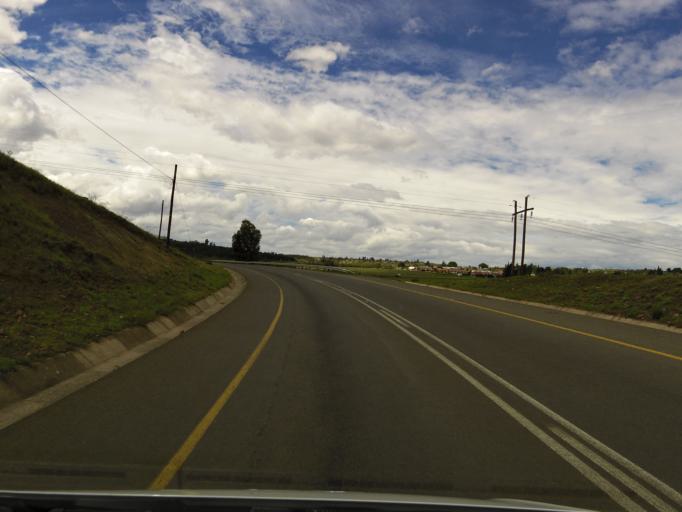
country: LS
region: Maseru
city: Maseru
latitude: -29.3922
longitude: 27.5470
